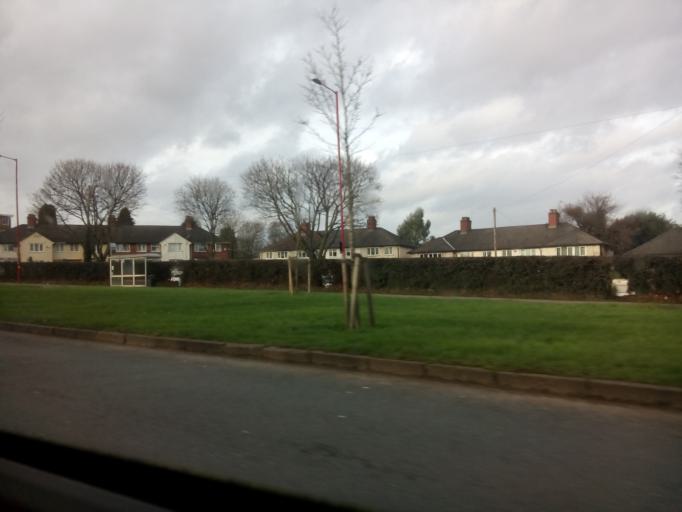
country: GB
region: England
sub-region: Worcestershire
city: Barnt Green
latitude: 52.3954
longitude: -1.9990
